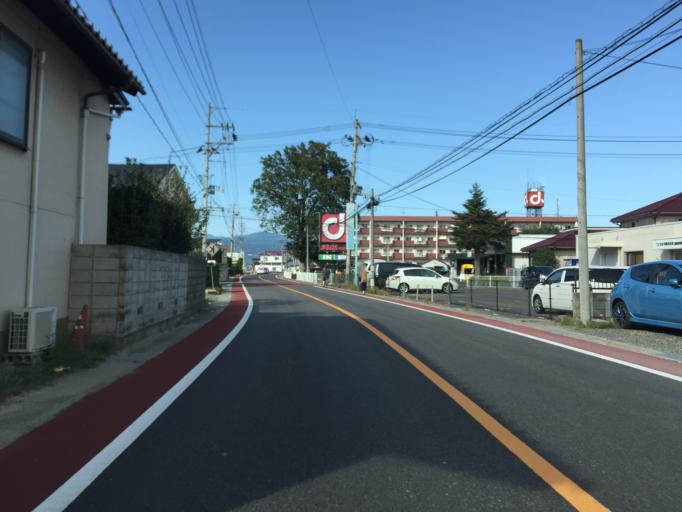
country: JP
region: Fukushima
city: Fukushima-shi
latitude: 37.7749
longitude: 140.4973
